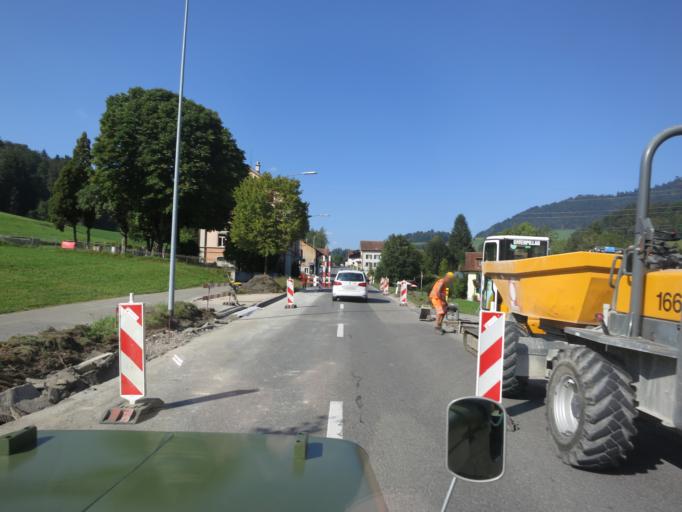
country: CH
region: Zurich
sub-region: Bezirk Hinwil
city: Wald
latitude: 47.2925
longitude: 8.9165
